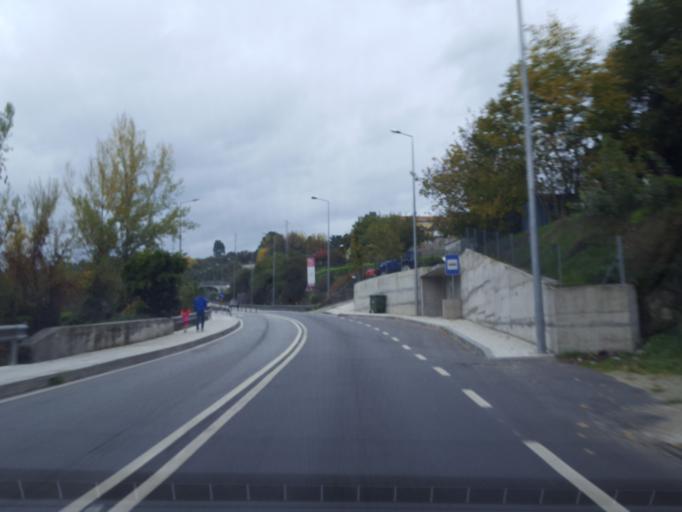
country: PT
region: Porto
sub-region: Marco de Canaveses
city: Marco de Canavezes
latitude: 41.1977
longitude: -8.1616
